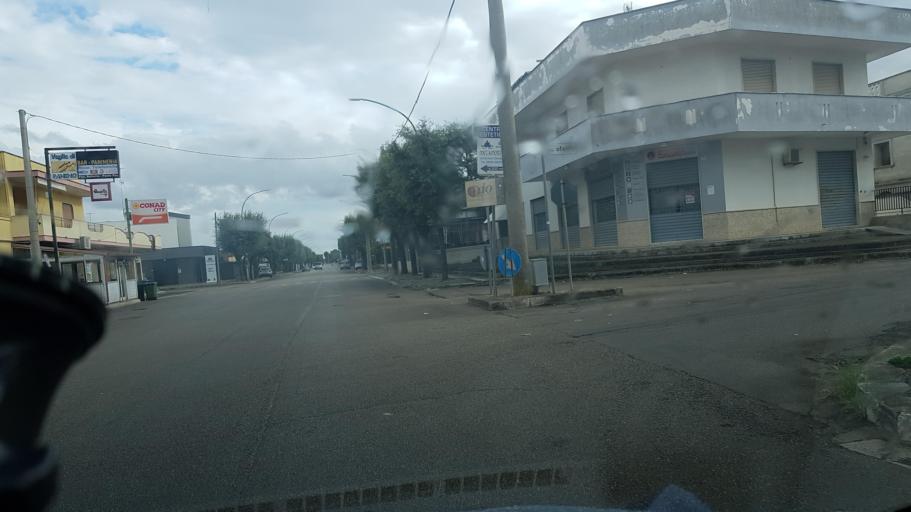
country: IT
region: Apulia
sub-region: Provincia di Lecce
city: Surbo
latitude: 40.3876
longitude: 18.1333
